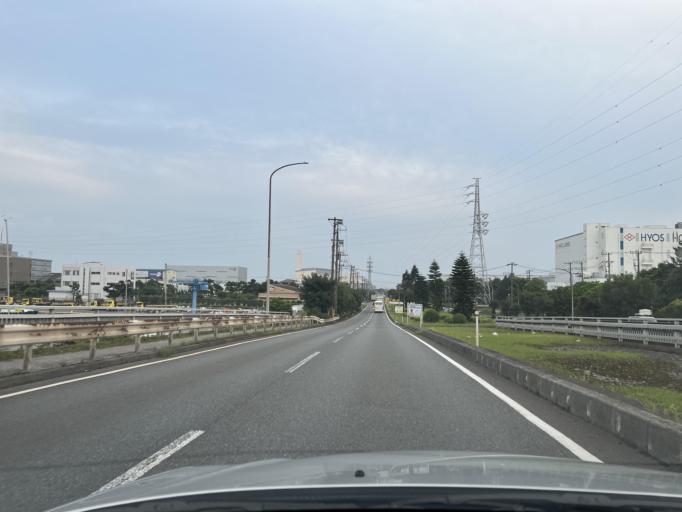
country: JP
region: Chiba
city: Funabashi
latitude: 35.6807
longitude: 139.9630
